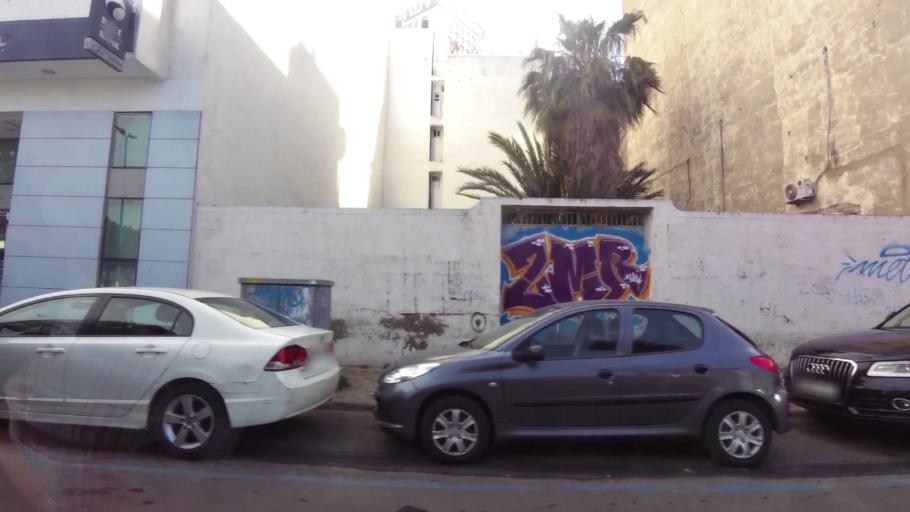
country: MA
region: Grand Casablanca
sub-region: Casablanca
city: Casablanca
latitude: 33.5853
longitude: -7.6337
